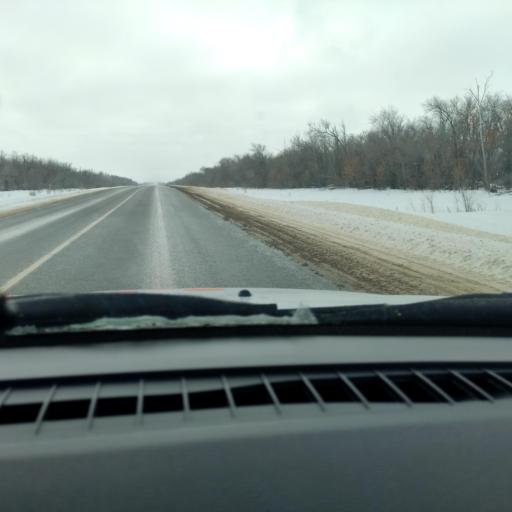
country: RU
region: Samara
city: Dubovyy Umet
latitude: 52.7452
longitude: 50.4926
